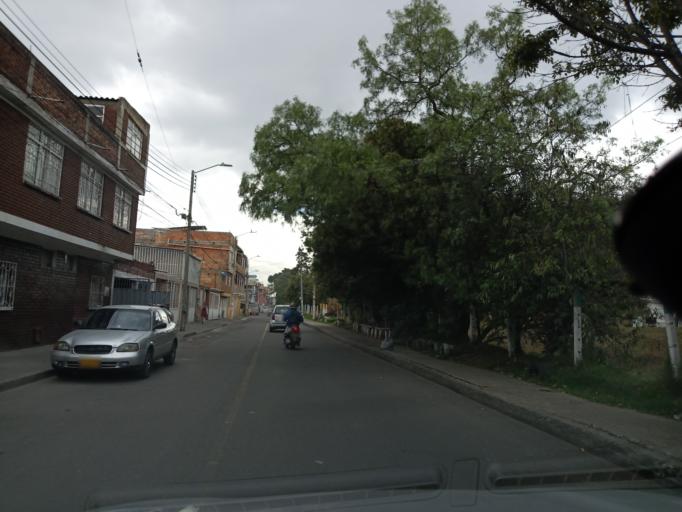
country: CO
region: Bogota D.C.
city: Bogota
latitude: 4.5801
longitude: -74.1118
